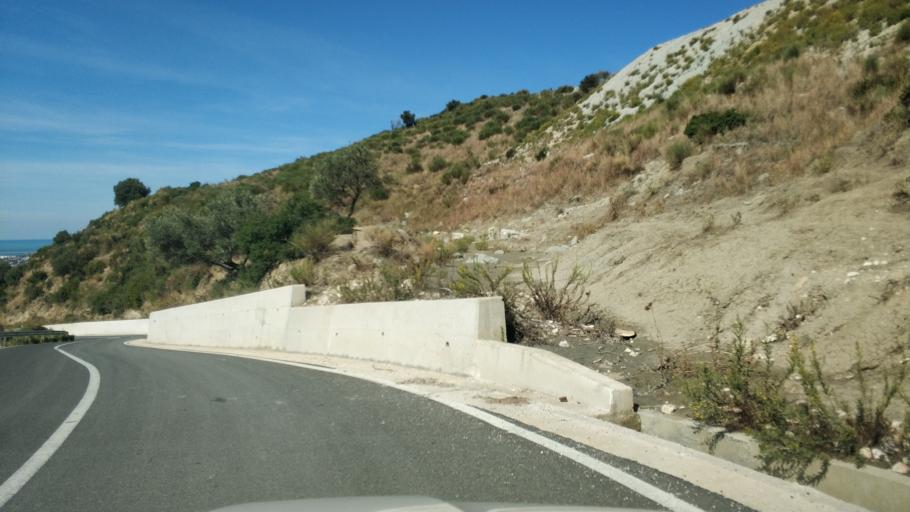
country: AL
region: Vlore
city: Vlore
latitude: 40.4565
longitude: 19.5137
